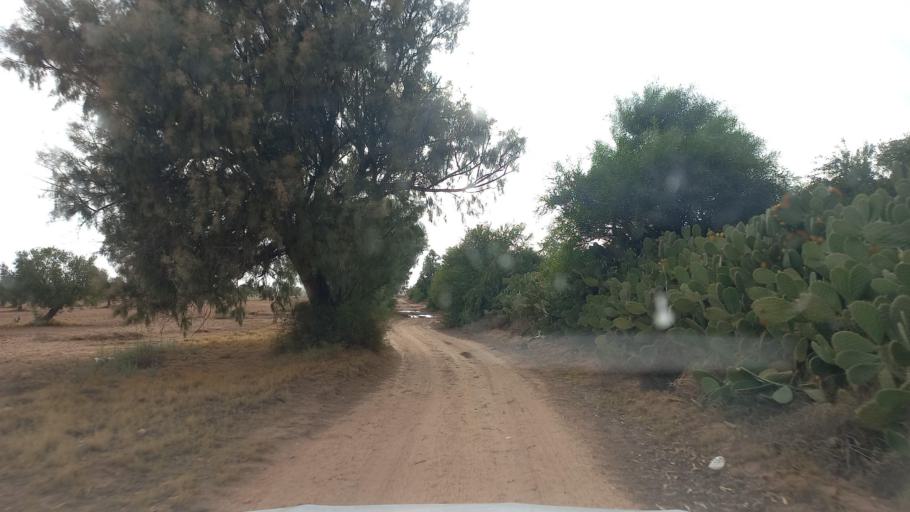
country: TN
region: Al Qasrayn
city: Sbiba
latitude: 35.2937
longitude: 9.0598
